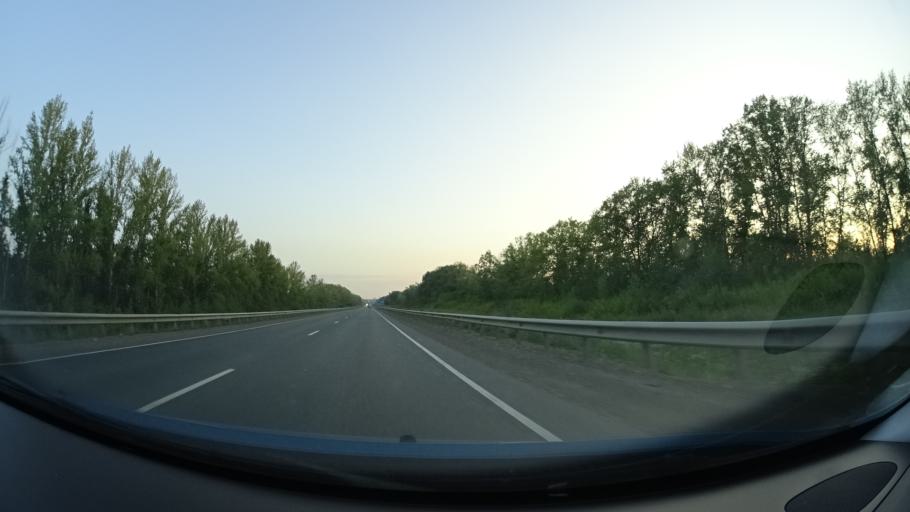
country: RU
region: Samara
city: Sukhodol
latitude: 53.8763
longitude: 51.2181
